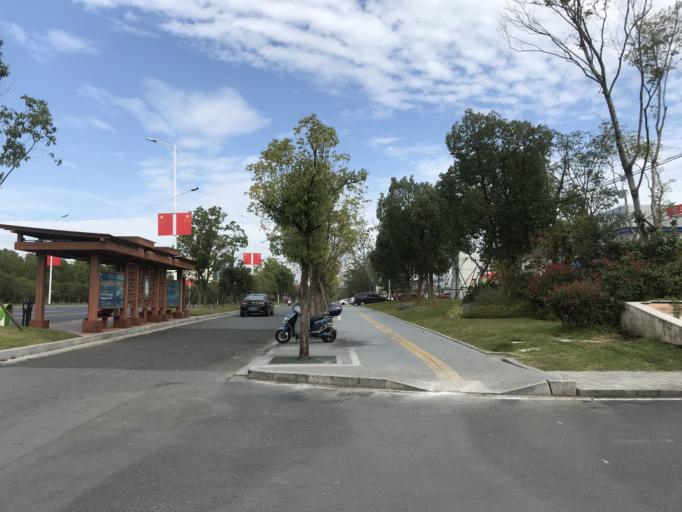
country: CN
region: Anhui Sheng
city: Xintan
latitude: 29.7689
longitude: 118.2592
